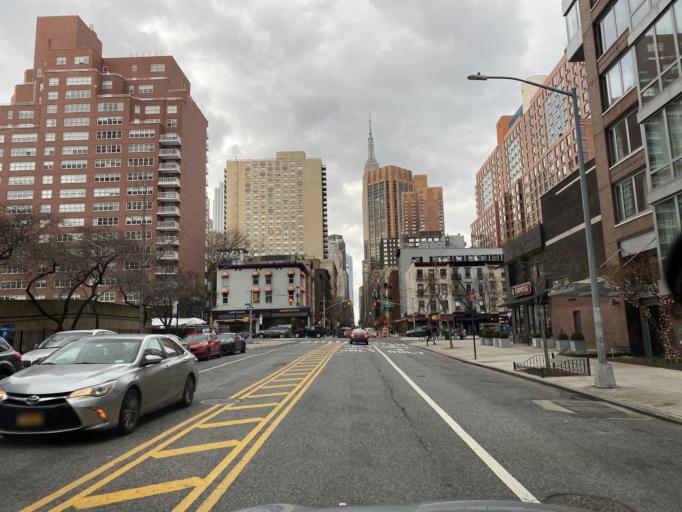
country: US
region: New York
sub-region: Queens County
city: Long Island City
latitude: 40.7438
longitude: -73.9756
